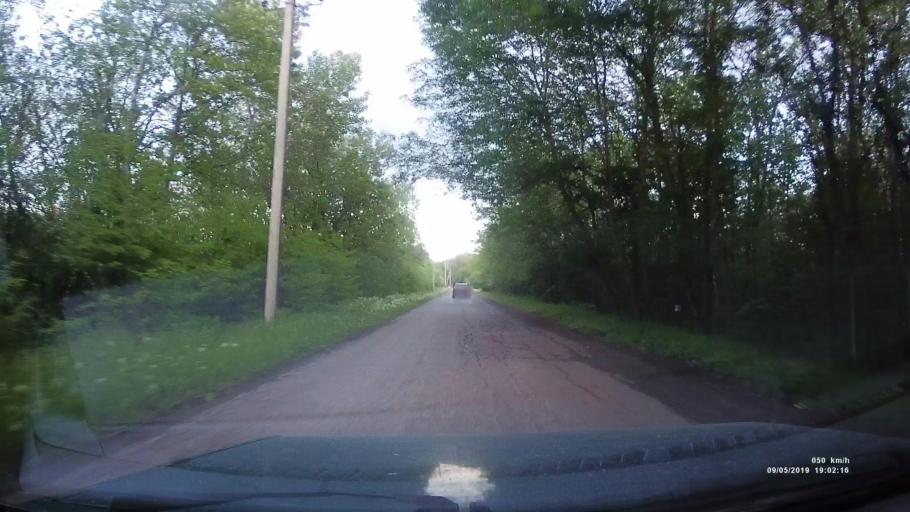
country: RU
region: Krasnodarskiy
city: Kanelovskaya
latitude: 46.7456
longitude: 39.1511
